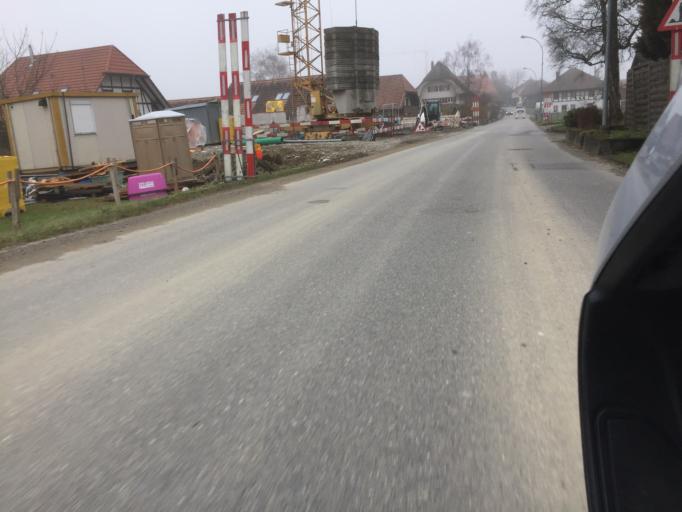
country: CH
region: Bern
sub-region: Seeland District
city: Grossaffoltern
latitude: 47.0877
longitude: 7.3763
